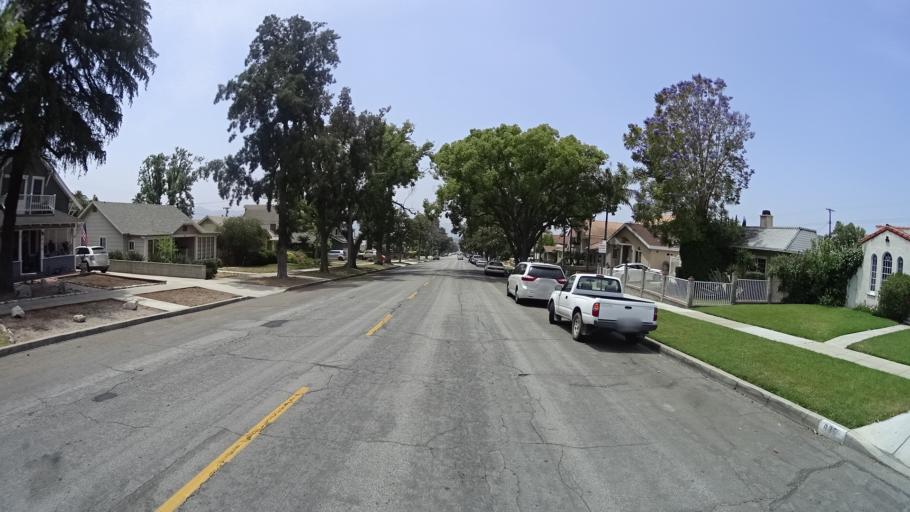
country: US
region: California
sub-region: Los Angeles County
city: Burbank
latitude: 34.1911
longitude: -118.3033
